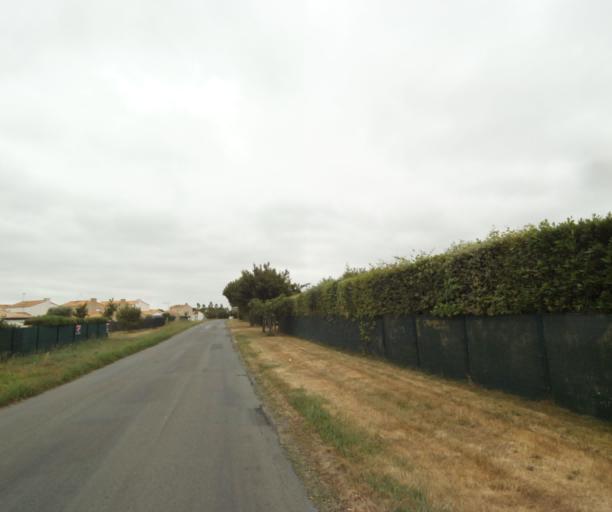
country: FR
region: Pays de la Loire
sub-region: Departement de la Vendee
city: Chateau-d'Olonne
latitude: 46.5080
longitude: -1.7517
